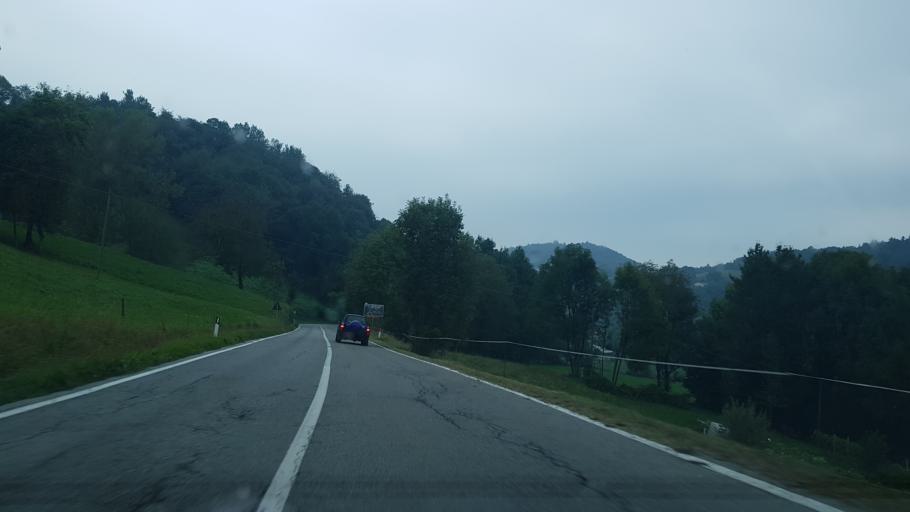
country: IT
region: Piedmont
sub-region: Provincia di Cuneo
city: Frabosa Sottana
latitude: 44.3179
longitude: 7.8031
